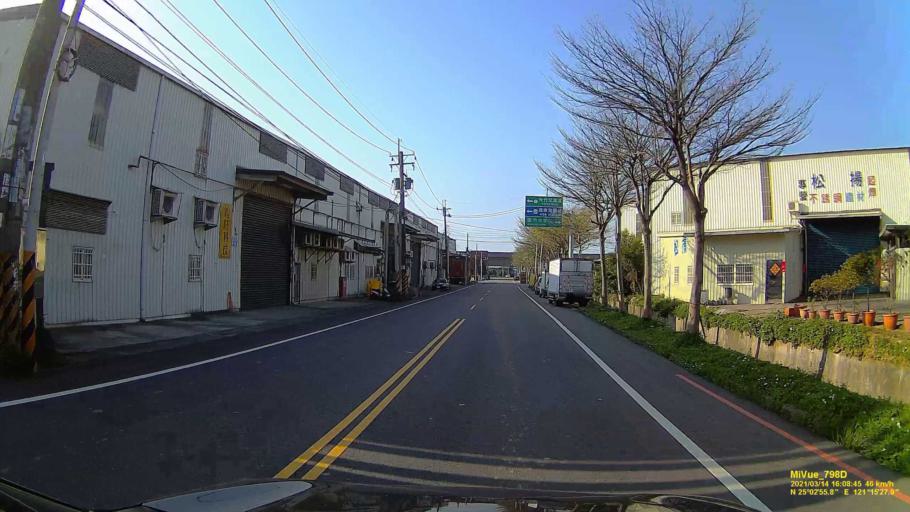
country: TW
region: Taiwan
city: Taoyuan City
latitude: 25.0490
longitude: 121.2577
